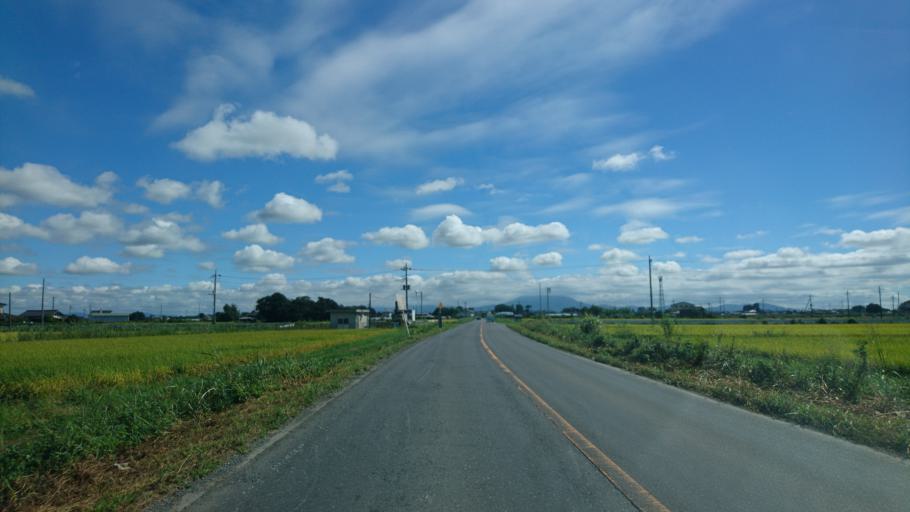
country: JP
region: Ibaraki
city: Yuki
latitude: 36.2168
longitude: 139.9031
